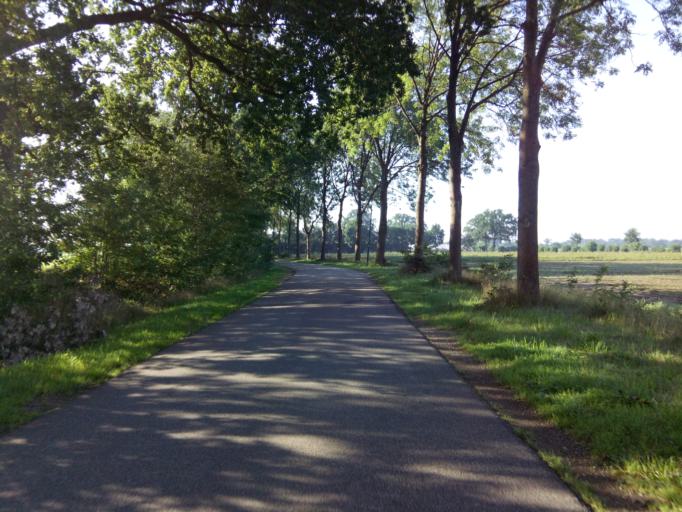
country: NL
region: Utrecht
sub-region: Gemeente Woudenberg
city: Woudenberg
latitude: 52.0702
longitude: 5.4553
